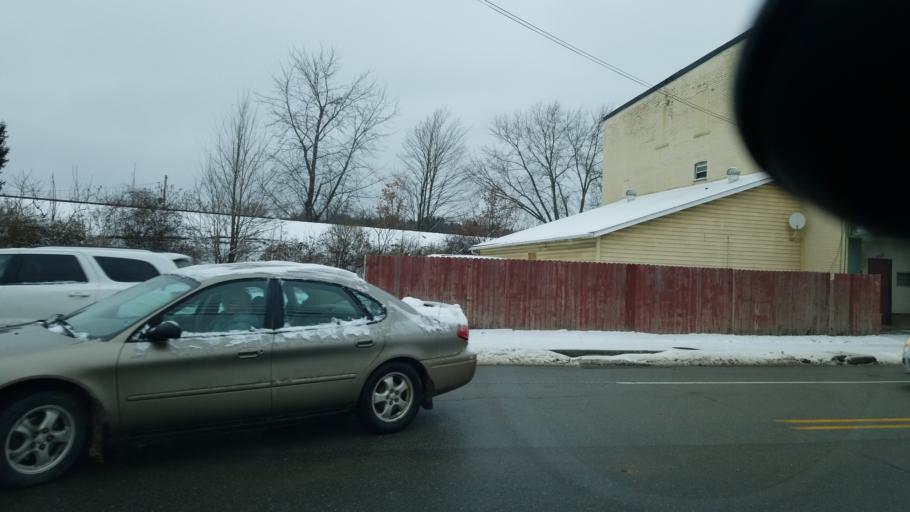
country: US
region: Pennsylvania
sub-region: Jefferson County
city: Punxsutawney
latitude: 40.9422
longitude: -78.9815
